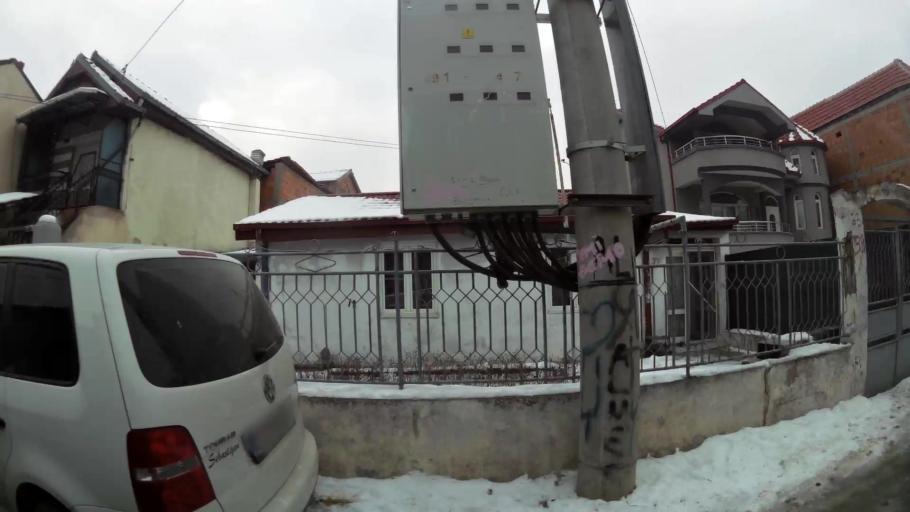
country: MK
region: Suto Orizari
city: Suto Orizare
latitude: 42.0458
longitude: 21.4216
